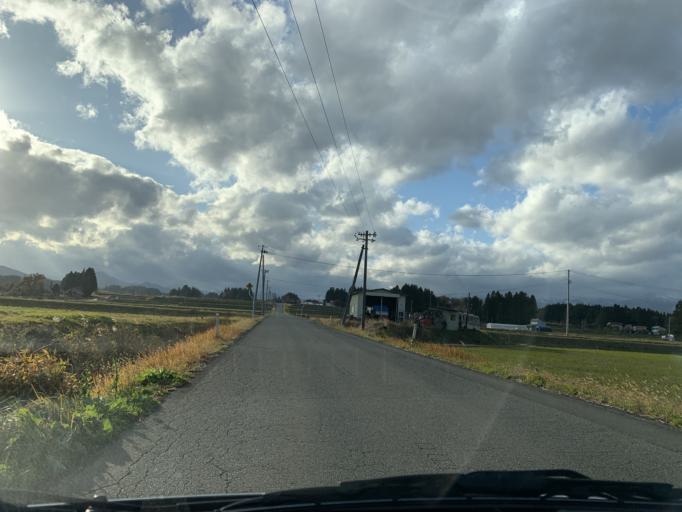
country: JP
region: Iwate
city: Mizusawa
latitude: 39.1110
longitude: 141.0438
